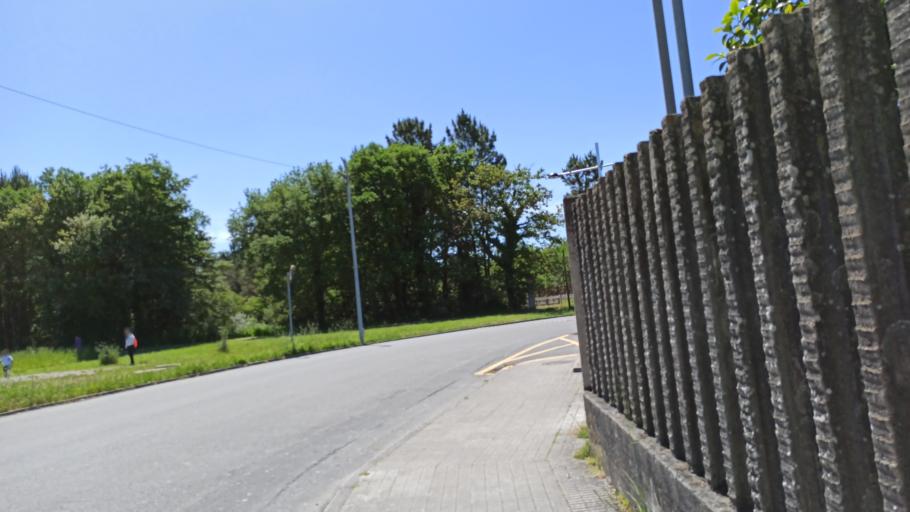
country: ES
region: Galicia
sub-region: Provincia da Coruna
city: Negreira
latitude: 42.9131
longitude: -8.7328
